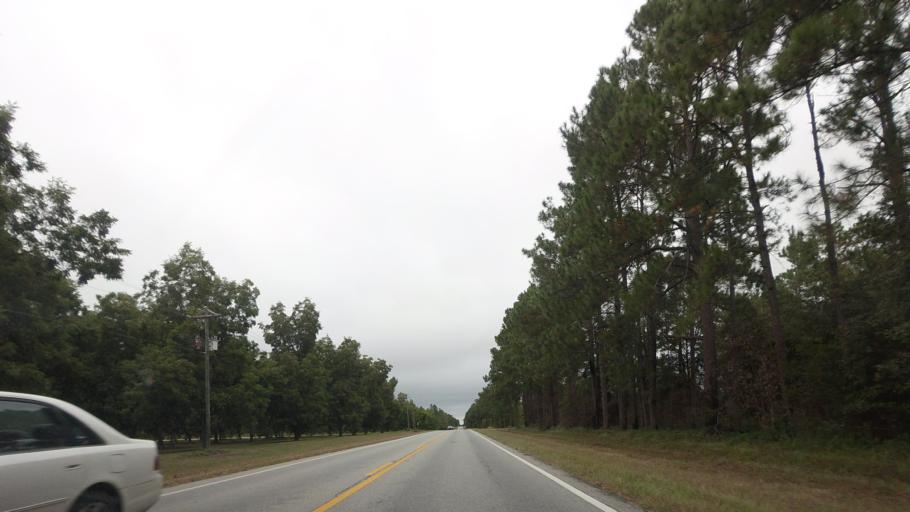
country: US
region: Georgia
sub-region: Berrien County
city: Ray City
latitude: 31.1020
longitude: -83.2083
